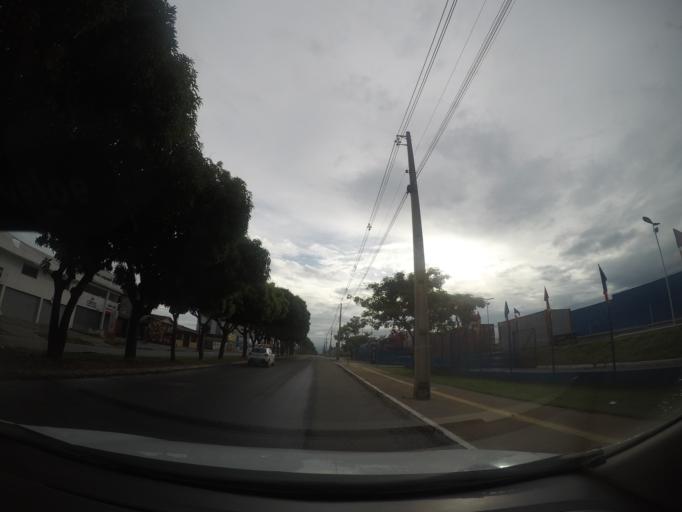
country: BR
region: Goias
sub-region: Goiania
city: Goiania
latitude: -16.7425
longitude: -49.2824
